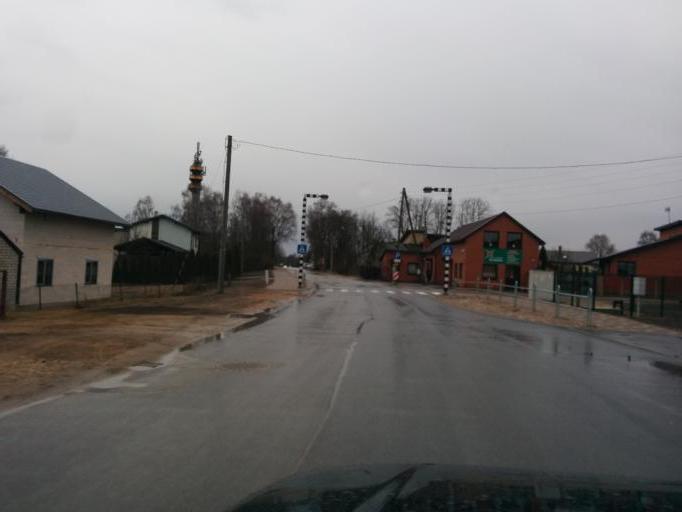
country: LV
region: Kekava
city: Balozi
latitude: 56.8758
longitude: 24.1785
